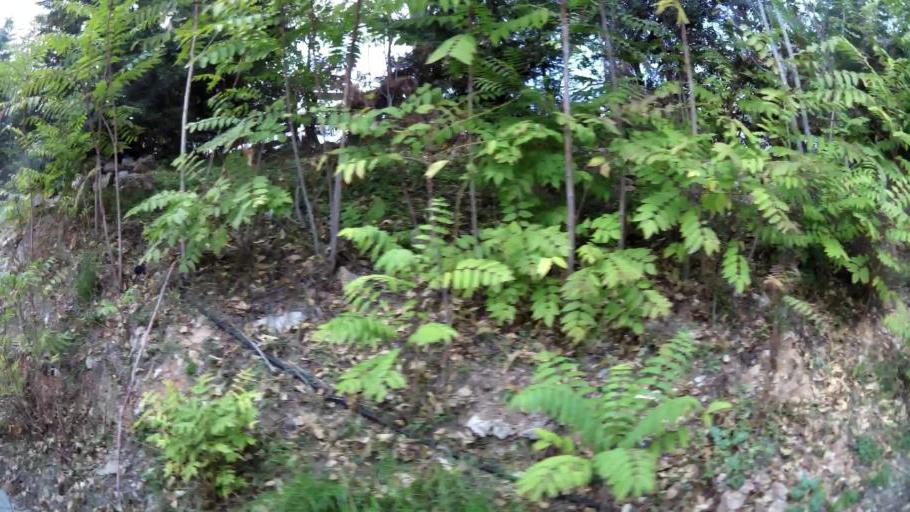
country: GR
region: Attica
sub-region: Nomarchia Athinas
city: Petroupolis
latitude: 38.0494
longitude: 23.6865
